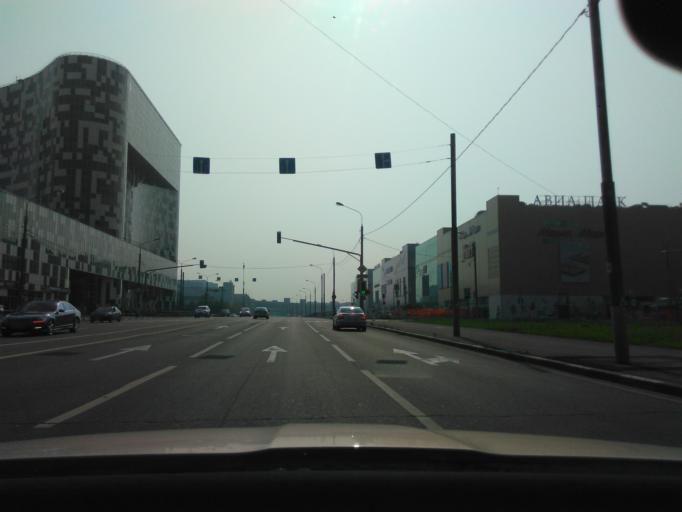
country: RU
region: Moscow
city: Sokol
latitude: 55.7922
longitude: 37.5253
